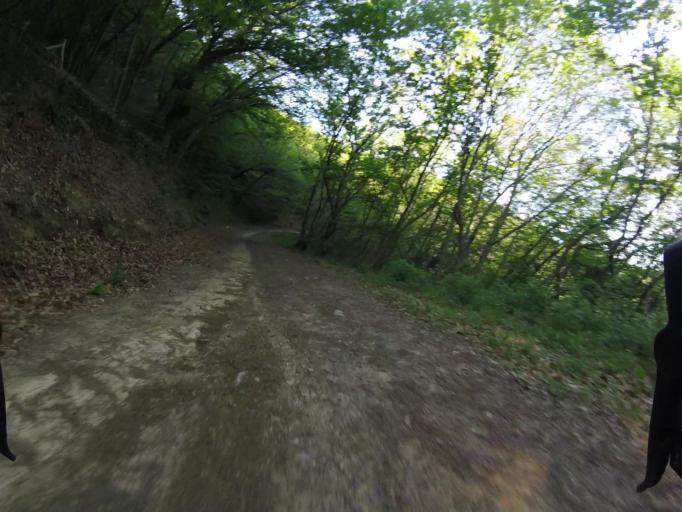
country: ES
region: Basque Country
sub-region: Provincia de Guipuzcoa
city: Fuenterrabia
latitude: 43.3605
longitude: -1.8248
